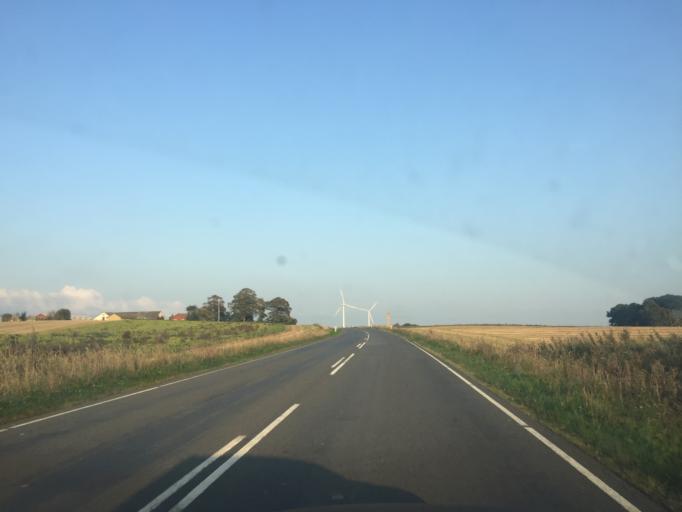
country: DK
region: Zealand
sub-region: Soro Kommune
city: Dianalund
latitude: 55.5269
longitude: 11.5401
